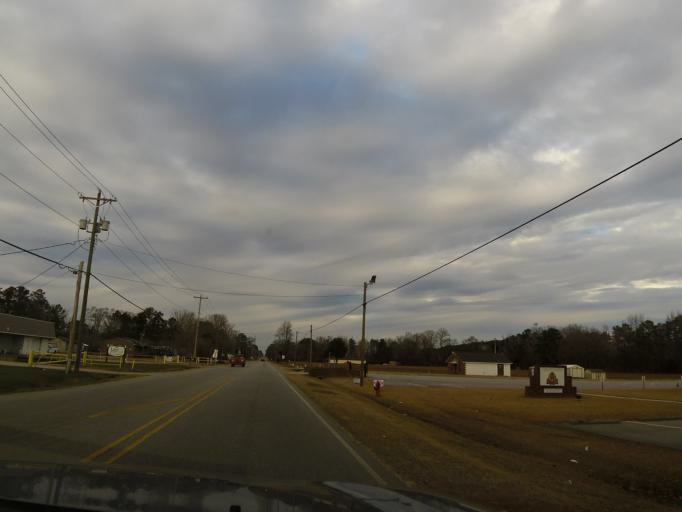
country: US
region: North Carolina
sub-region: Nash County
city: Sharpsburg
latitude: 35.8886
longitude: -77.8196
